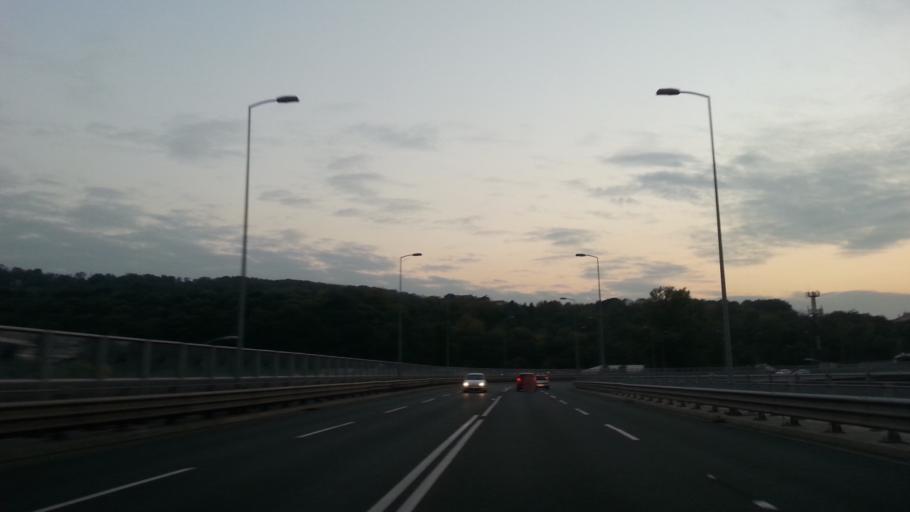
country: RS
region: Central Serbia
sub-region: Belgrade
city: Cukarica
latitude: 44.7847
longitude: 20.4308
